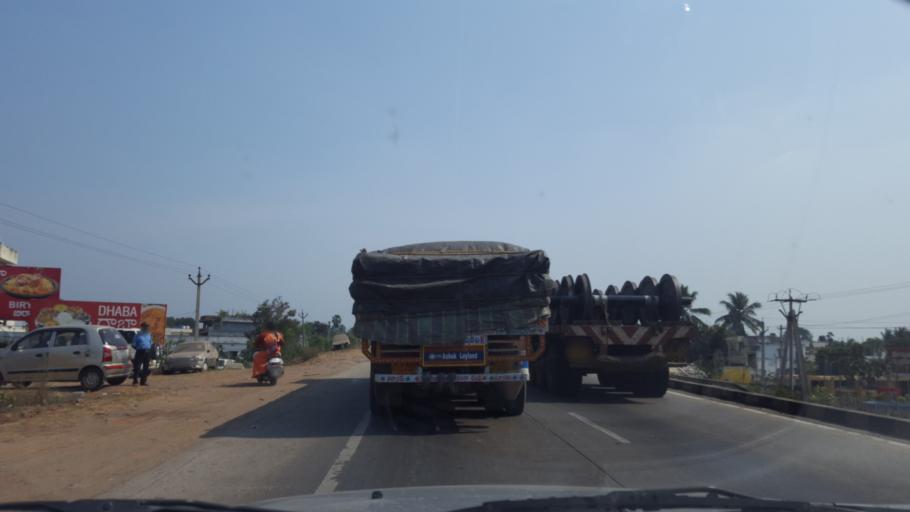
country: IN
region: Andhra Pradesh
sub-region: Vishakhapatnam
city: Anakapalle
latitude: 17.6816
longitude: 82.9887
